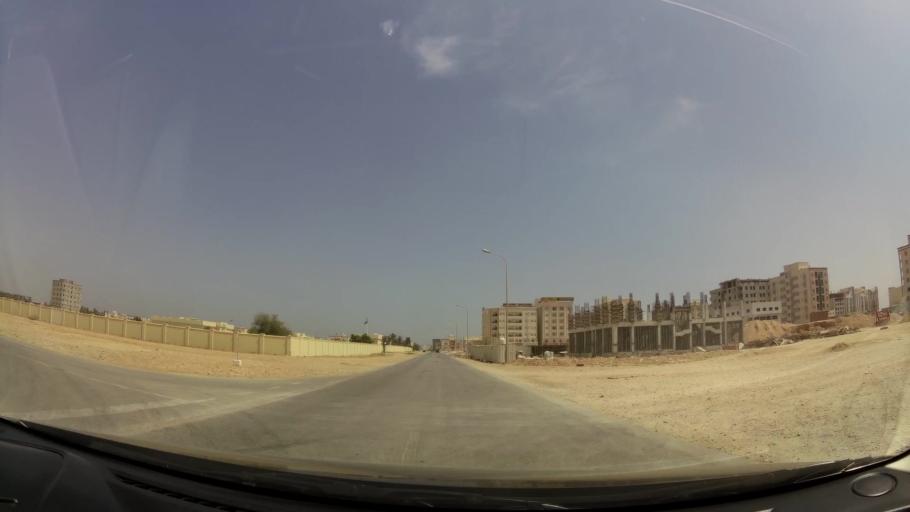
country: OM
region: Zufar
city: Salalah
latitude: 17.0530
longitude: 54.1574
